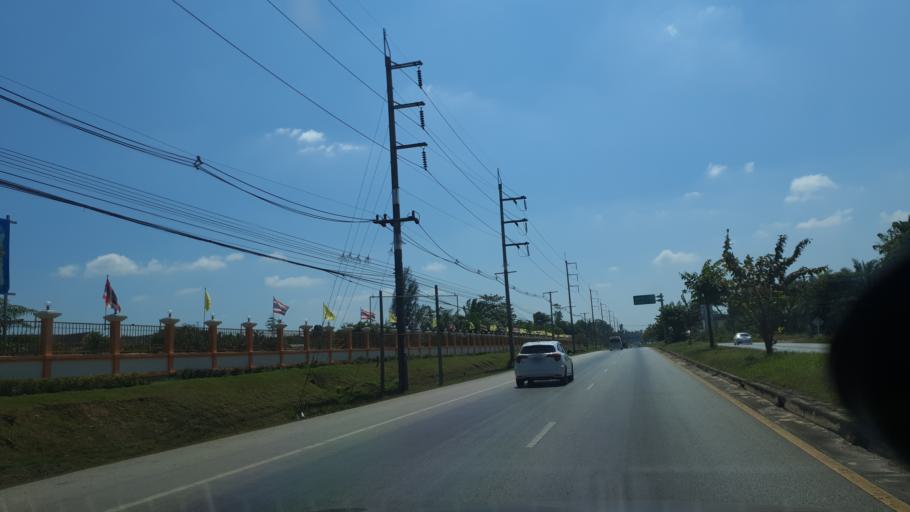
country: TH
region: Krabi
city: Khlong Thom
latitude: 7.9780
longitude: 99.1387
